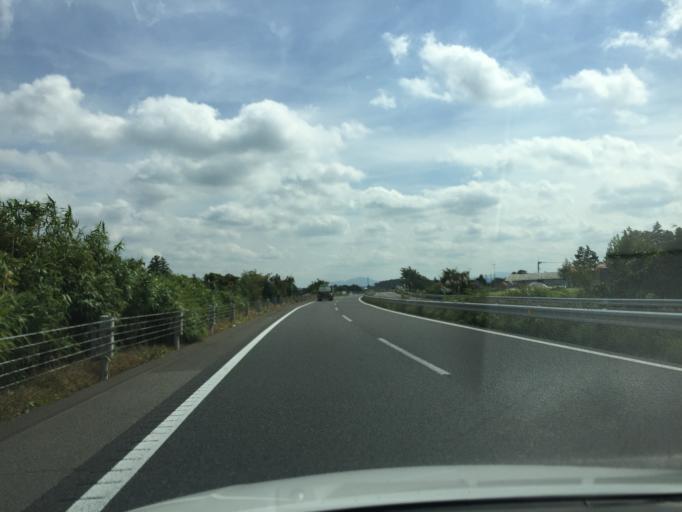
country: JP
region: Fukushima
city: Koriyama
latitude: 37.4556
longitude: 140.3987
